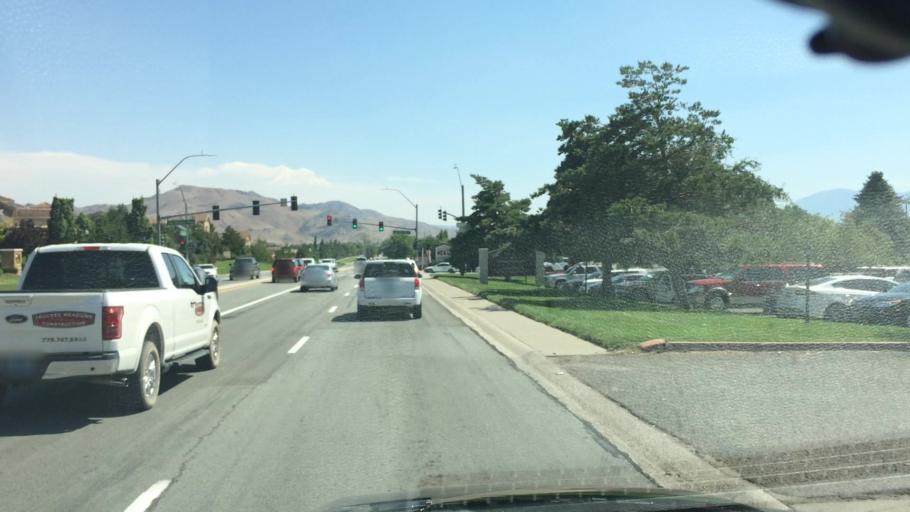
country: US
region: Nevada
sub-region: Washoe County
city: Sparks
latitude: 39.5593
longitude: -119.7057
